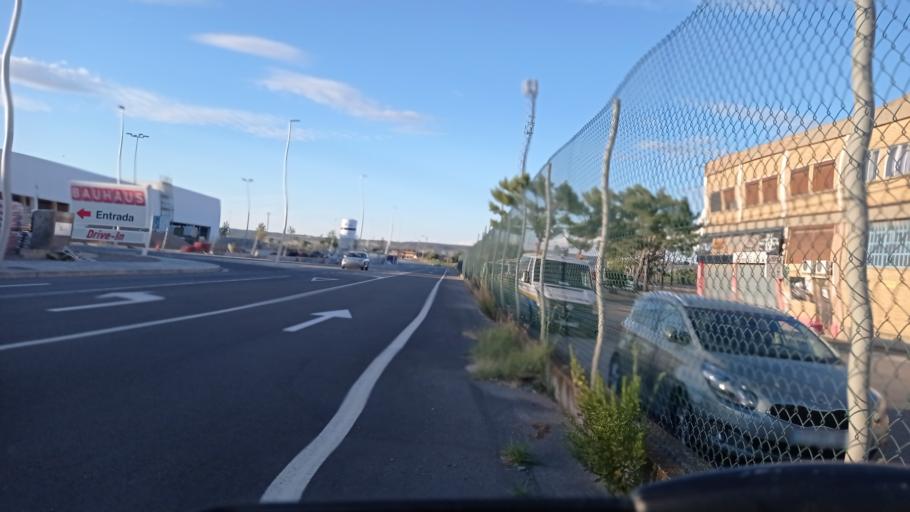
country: ES
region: Aragon
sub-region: Provincia de Zaragoza
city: Oliver-Valdefierro, Oliver, Valdefierro
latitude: 41.6746
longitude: -0.9501
